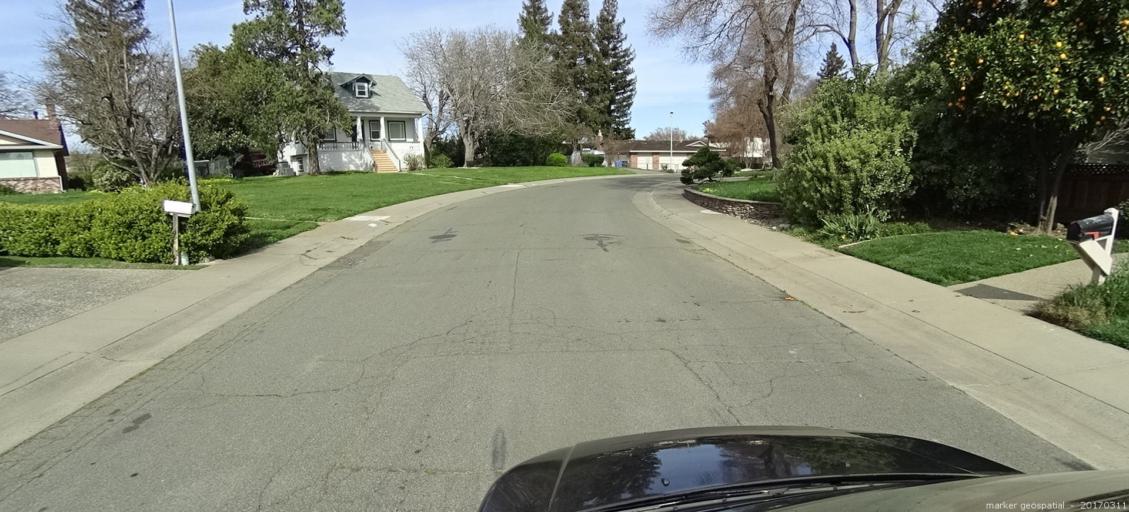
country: US
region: California
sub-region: Yolo County
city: West Sacramento
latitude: 38.5009
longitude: -121.5566
